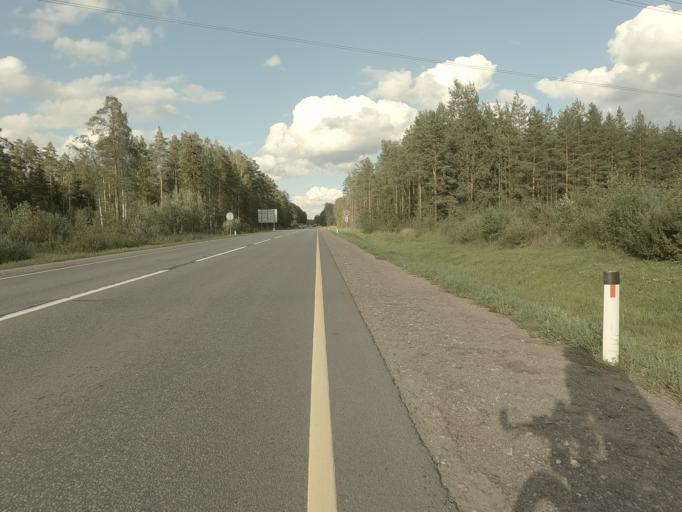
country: RU
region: Leningrad
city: Mga
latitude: 59.7095
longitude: 31.0210
